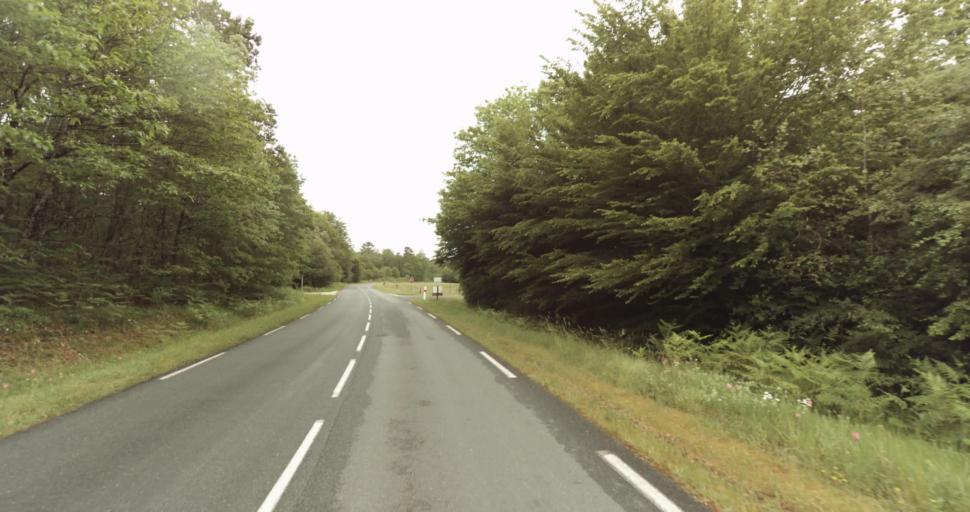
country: FR
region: Aquitaine
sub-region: Departement de la Dordogne
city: Belves
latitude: 44.6770
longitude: 0.9939
